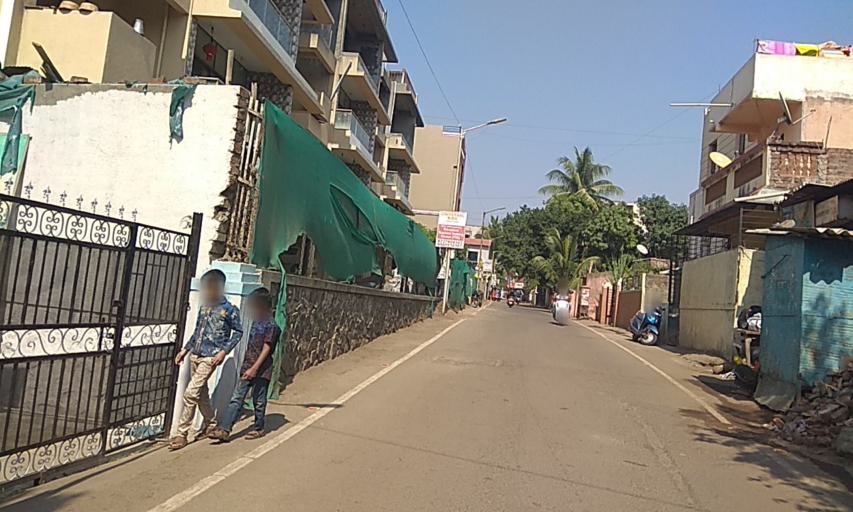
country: IN
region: Maharashtra
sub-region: Pune Division
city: Lohogaon
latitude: 18.5525
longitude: 73.9357
